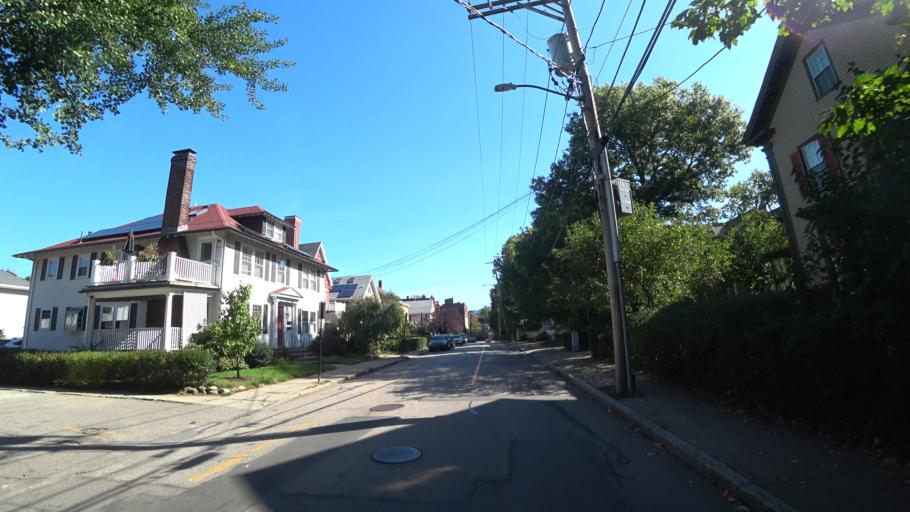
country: US
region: Massachusetts
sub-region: Norfolk County
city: Brookline
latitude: 42.3323
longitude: -71.1208
